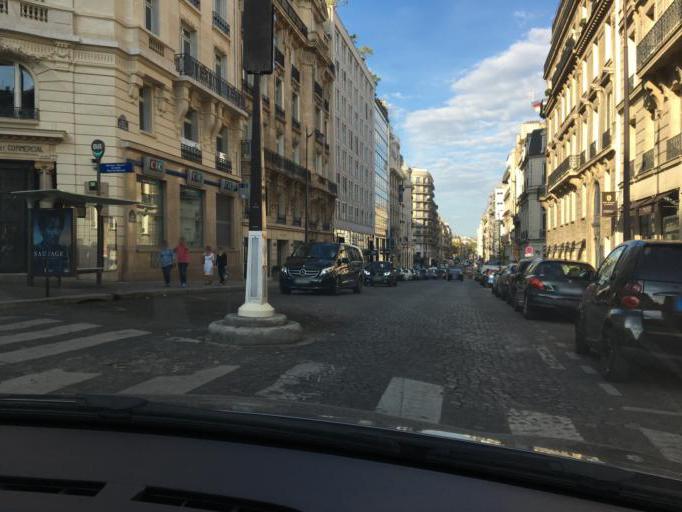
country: FR
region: Ile-de-France
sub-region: Departement des Hauts-de-Seine
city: Levallois-Perret
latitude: 48.8675
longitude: 2.2994
